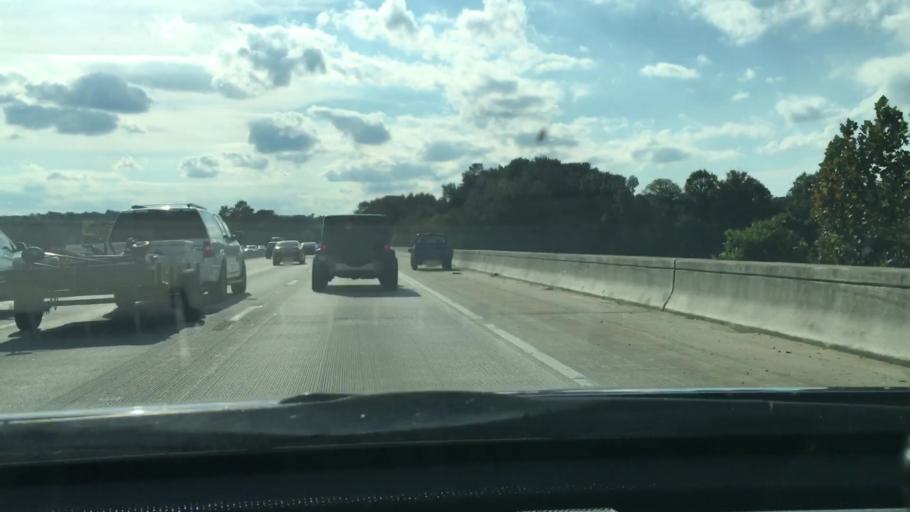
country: US
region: South Carolina
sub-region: Lexington County
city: West Columbia
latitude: 34.0486
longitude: -81.0721
